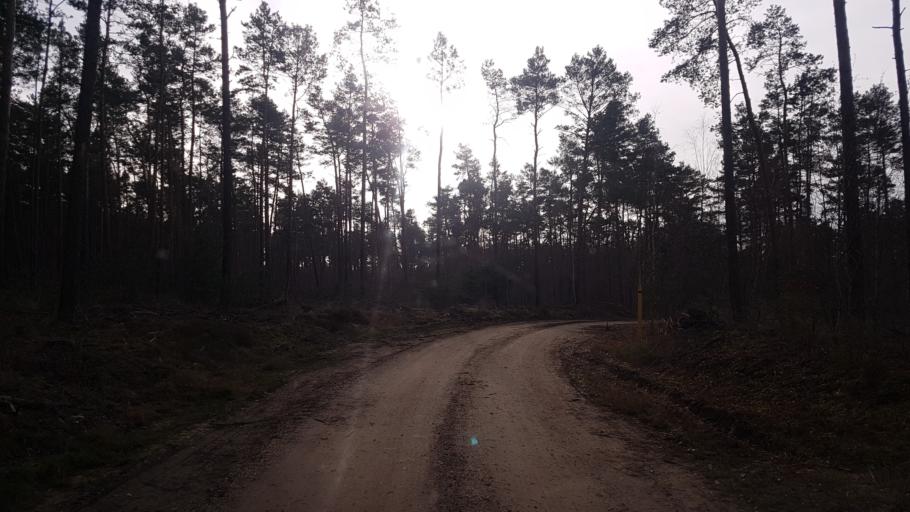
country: DE
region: Brandenburg
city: Schonborn
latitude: 51.5770
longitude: 13.4763
